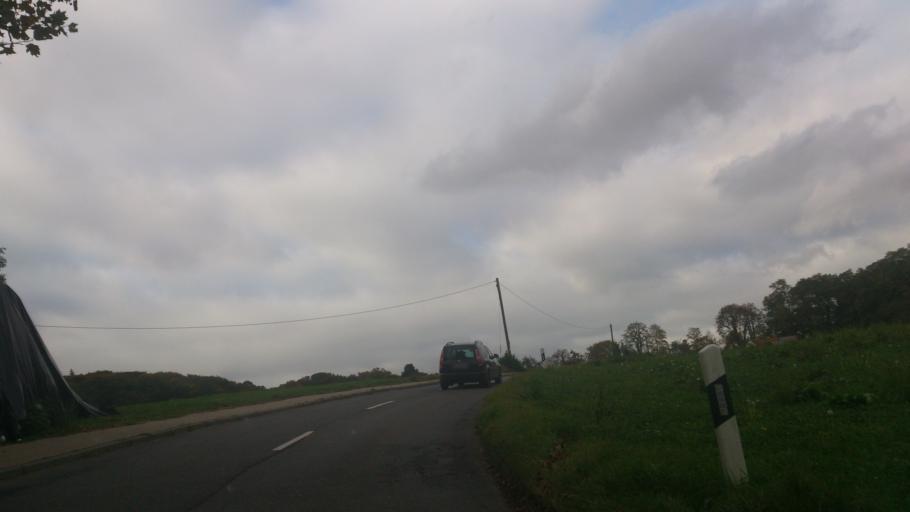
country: DE
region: Baden-Wuerttemberg
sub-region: Karlsruhe Region
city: Heidelberg
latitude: 49.3868
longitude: 8.7044
